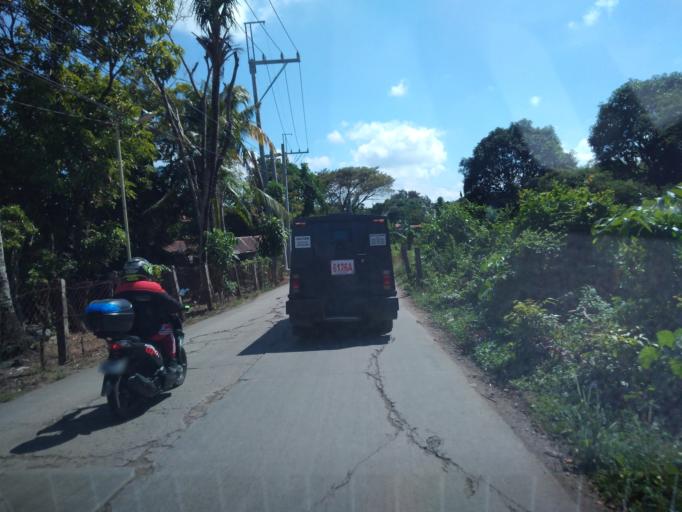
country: PH
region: Central Luzon
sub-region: Province of Bulacan
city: Balasing
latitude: 14.8591
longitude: 121.0278
